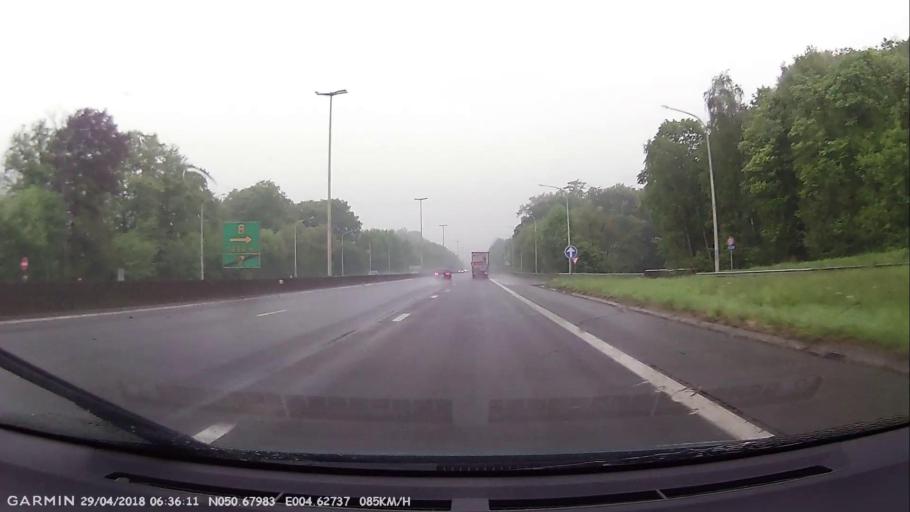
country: BE
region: Wallonia
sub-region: Province du Brabant Wallon
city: Louvain-la-Neuve
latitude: 50.6800
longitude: 4.6273
